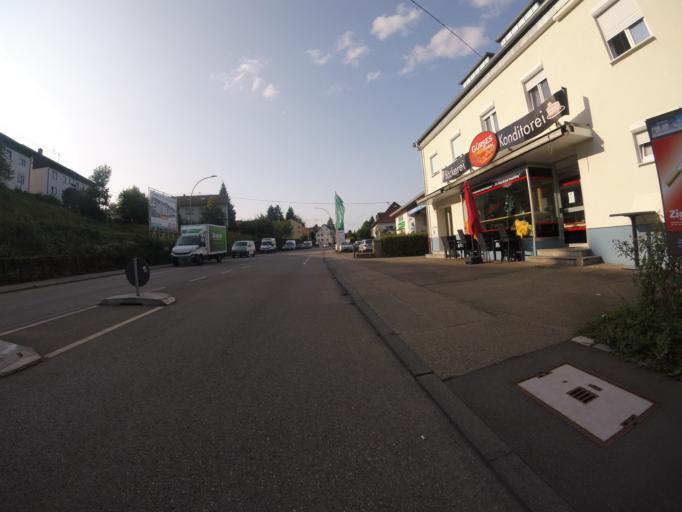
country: DE
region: Baden-Wuerttemberg
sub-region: Regierungsbezirk Stuttgart
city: Backnang
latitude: 48.9519
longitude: 9.4315
